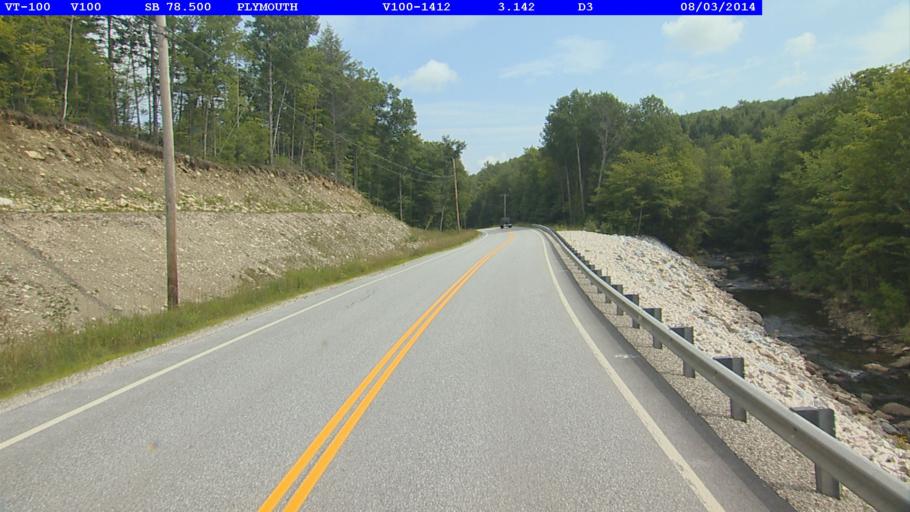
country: US
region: Vermont
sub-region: Windsor County
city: Woodstock
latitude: 43.5023
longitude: -72.7231
